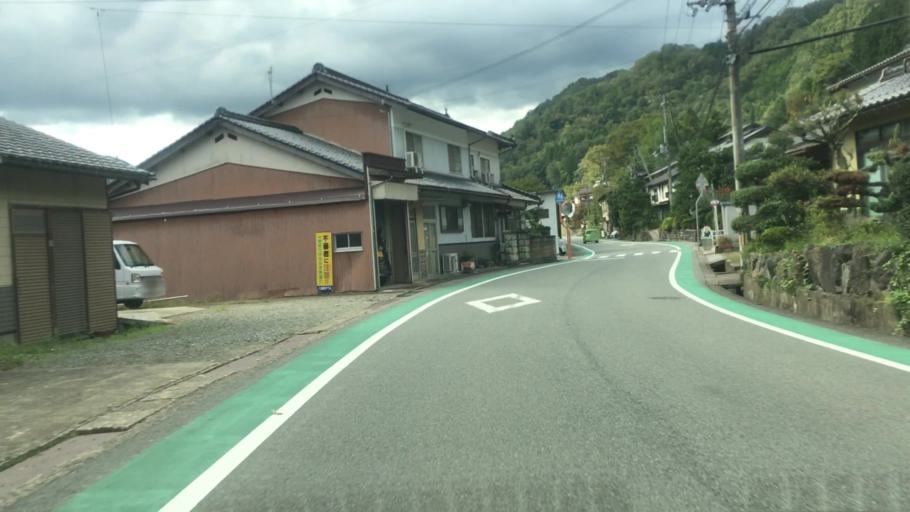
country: JP
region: Hyogo
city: Toyooka
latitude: 35.4083
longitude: 134.7560
